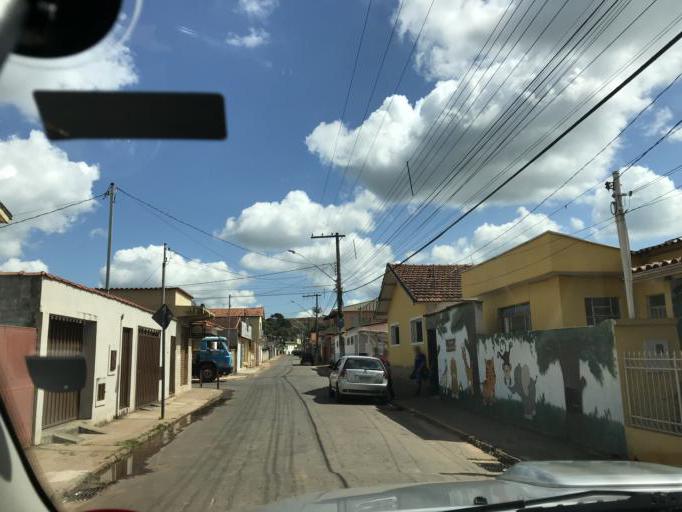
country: BR
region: Minas Gerais
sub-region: Campanha
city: Campanha
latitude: -21.8322
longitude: -45.4075
